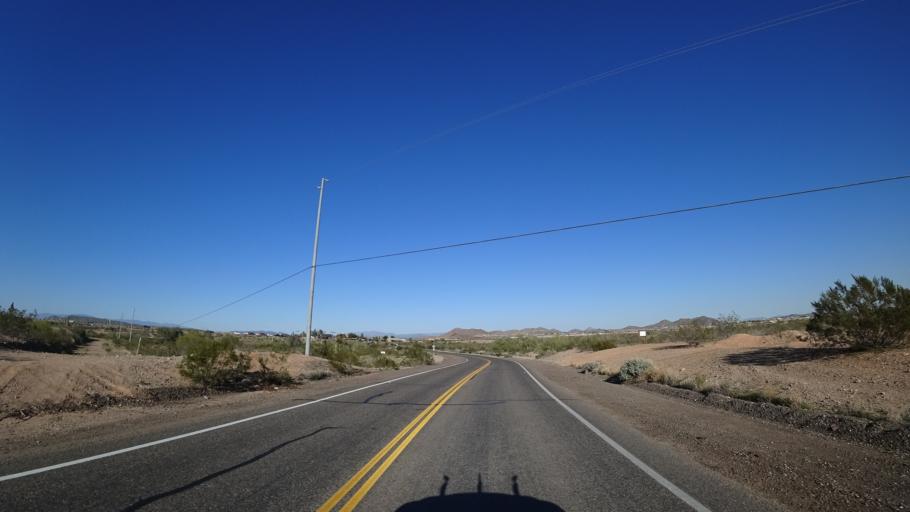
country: US
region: Arizona
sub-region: Maricopa County
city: Sun City West
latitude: 33.7109
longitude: -112.3082
